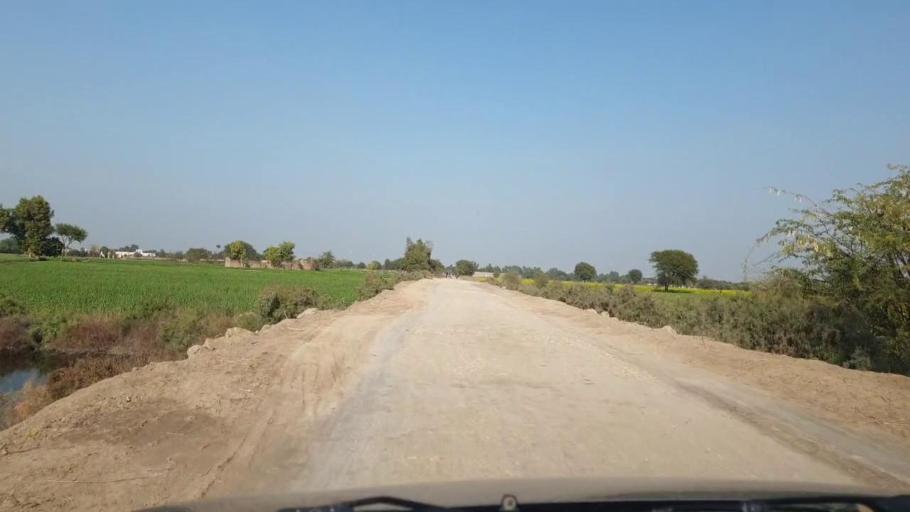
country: PK
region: Sindh
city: Jhol
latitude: 25.9365
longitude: 68.8795
